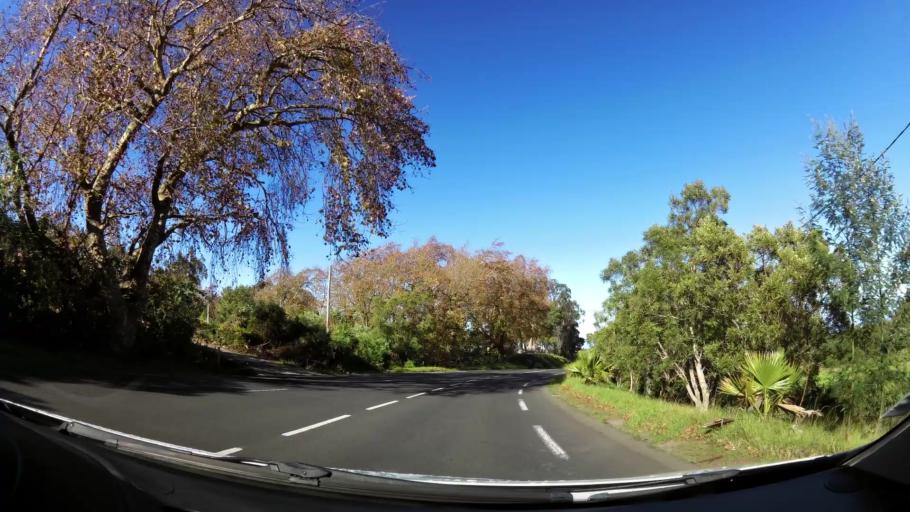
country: RE
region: Reunion
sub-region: Reunion
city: Le Tampon
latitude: -21.2113
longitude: 55.5668
